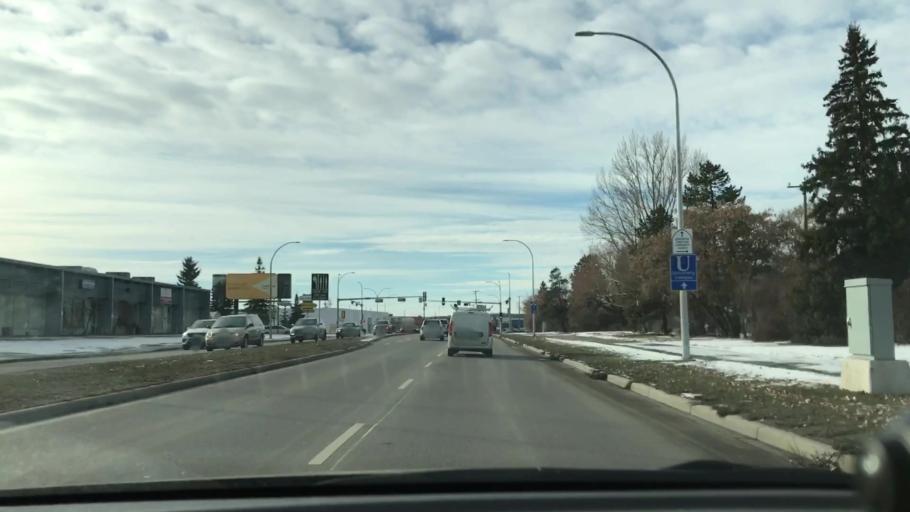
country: CA
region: Alberta
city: Edmonton
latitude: 53.5014
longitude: -113.4567
